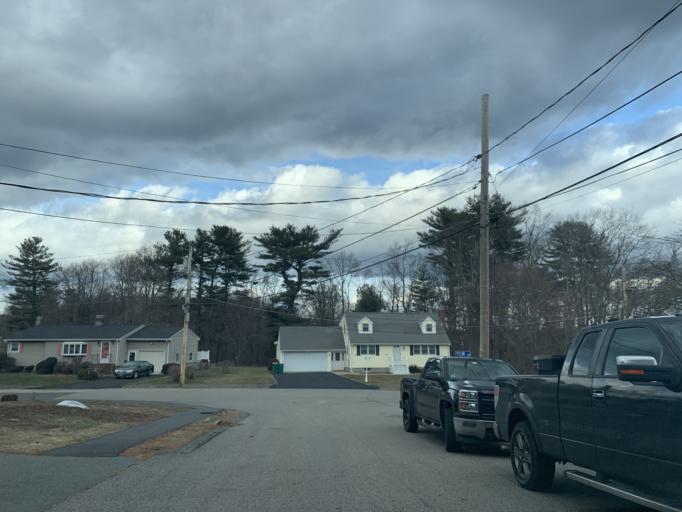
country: US
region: Massachusetts
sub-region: Norfolk County
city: Norwood
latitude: 42.1802
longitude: -71.1752
